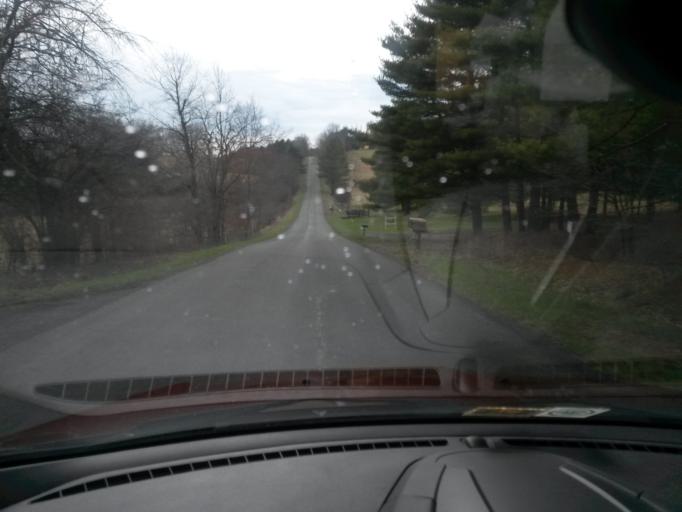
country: US
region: Virginia
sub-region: Bath County
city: Warm Springs
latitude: 38.0823
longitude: -79.8115
